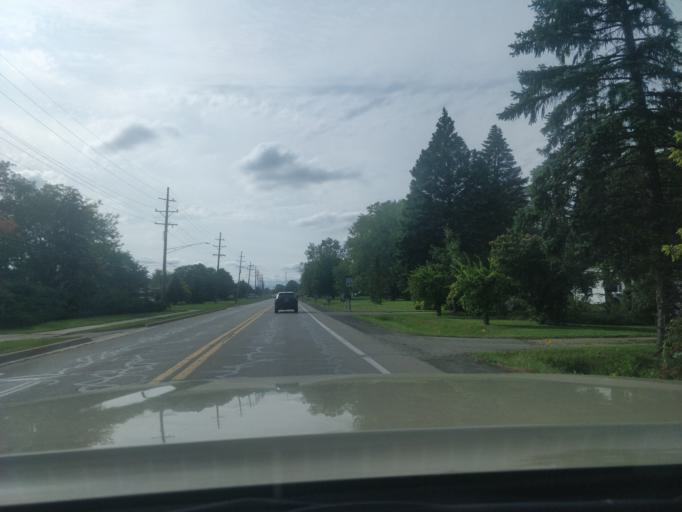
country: US
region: Michigan
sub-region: Wayne County
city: Woodhaven
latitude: 42.1542
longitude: -83.2472
